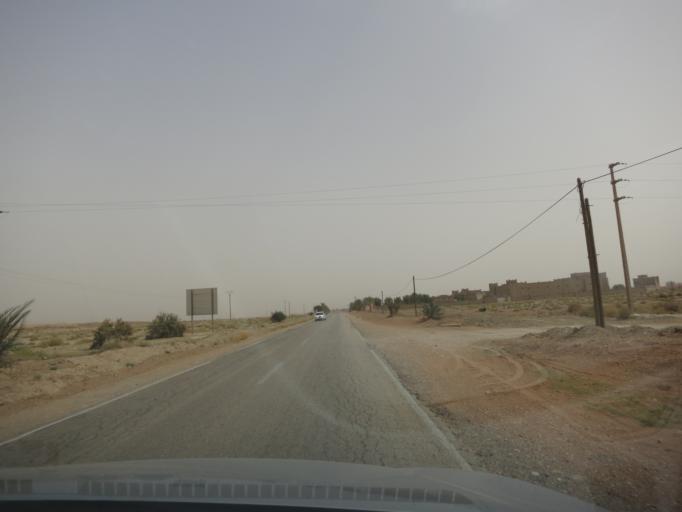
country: MA
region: Meknes-Tafilalet
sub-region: Errachidia
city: Jorf
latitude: 31.4879
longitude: -4.2119
